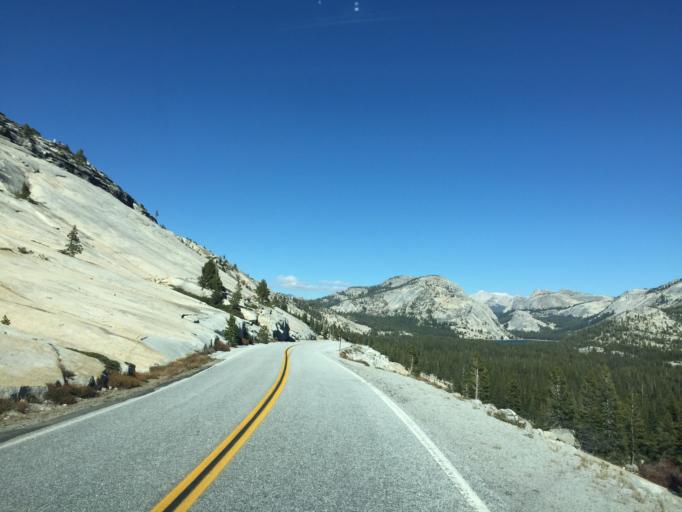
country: US
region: California
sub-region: Mariposa County
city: Yosemite Valley
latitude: 37.8114
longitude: -119.4839
